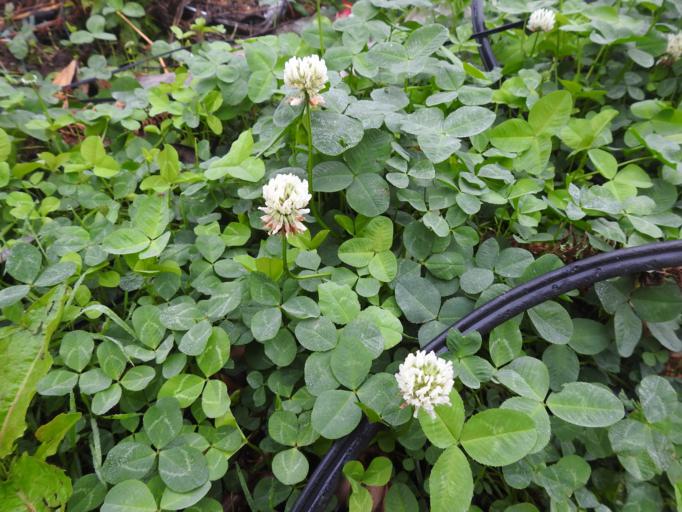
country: VN
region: Lao Cai
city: Sa Pa
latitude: 22.3378
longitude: 103.8325
